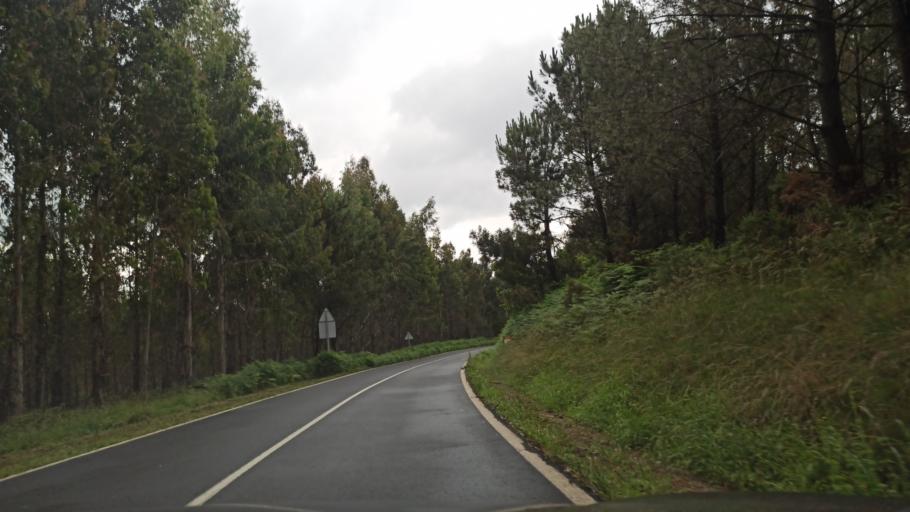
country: ES
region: Galicia
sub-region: Provincia da Coruna
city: Santiso
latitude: 42.7771
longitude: -8.0834
